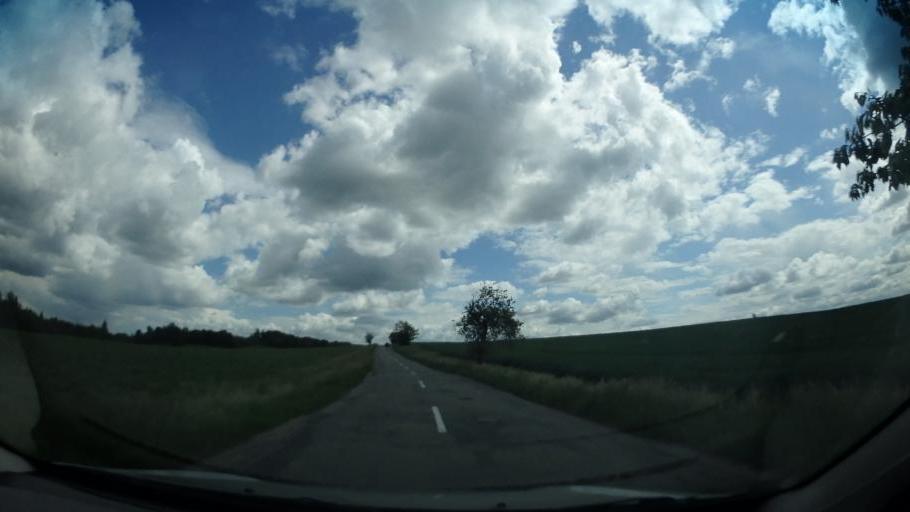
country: CZ
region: South Moravian
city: Velke Opatovice
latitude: 49.6207
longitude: 16.6041
